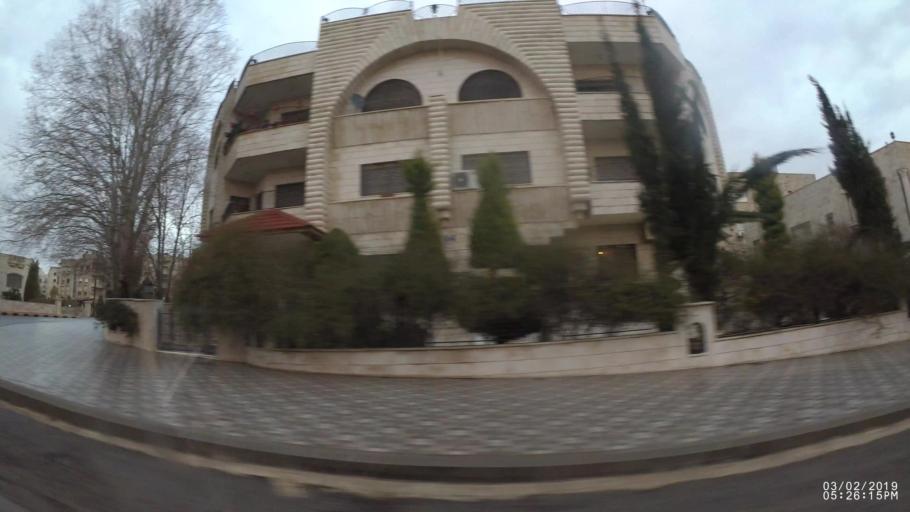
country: JO
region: Amman
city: Amman
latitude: 31.9870
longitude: 35.9103
